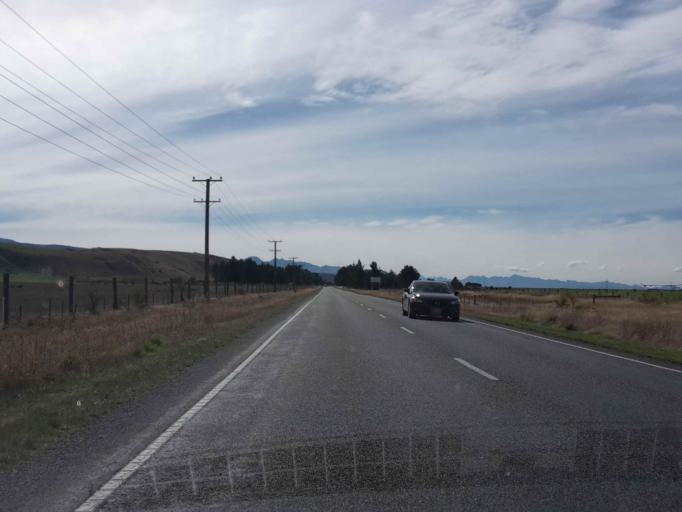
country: NZ
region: Otago
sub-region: Queenstown-Lakes District
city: Wanaka
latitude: -44.3912
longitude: 169.9958
